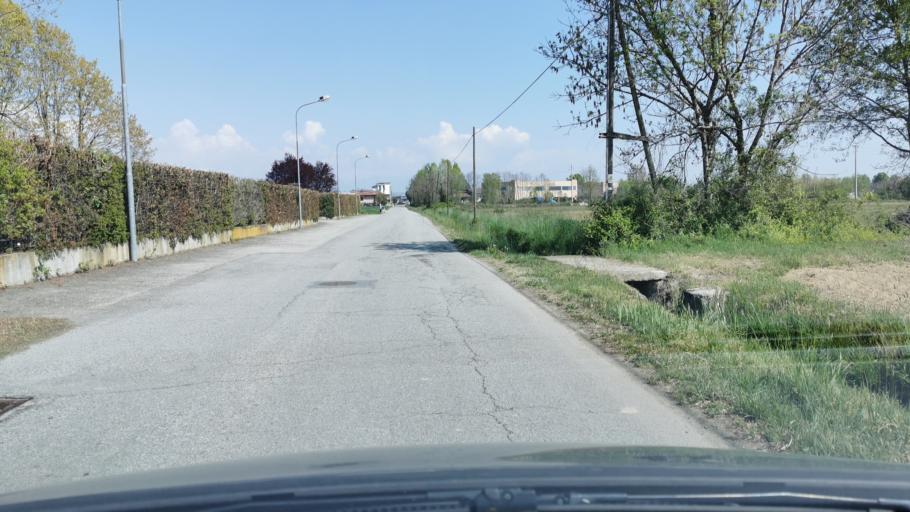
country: IT
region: Piedmont
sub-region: Provincia di Torino
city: Bosconero
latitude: 45.2623
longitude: 7.7584
